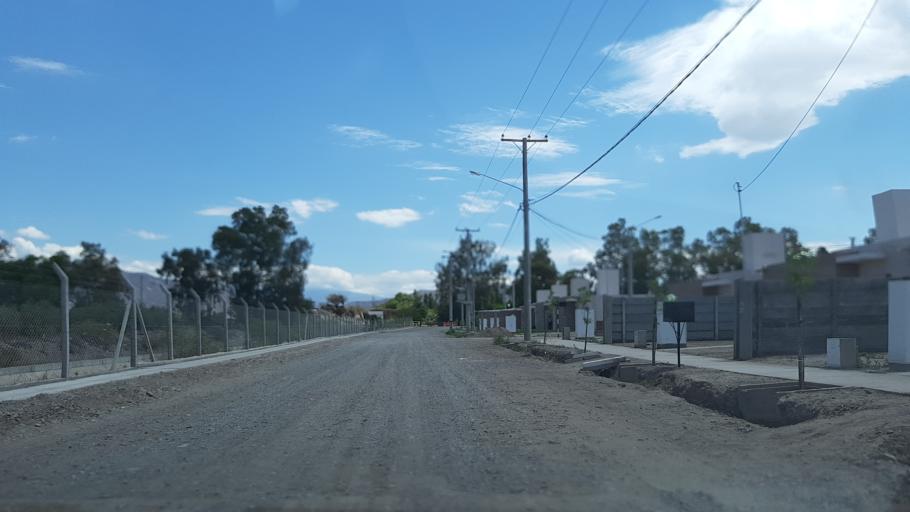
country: AR
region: San Juan
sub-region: Departamento de Rivadavia
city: Rivadavia
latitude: -31.5564
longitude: -68.6083
